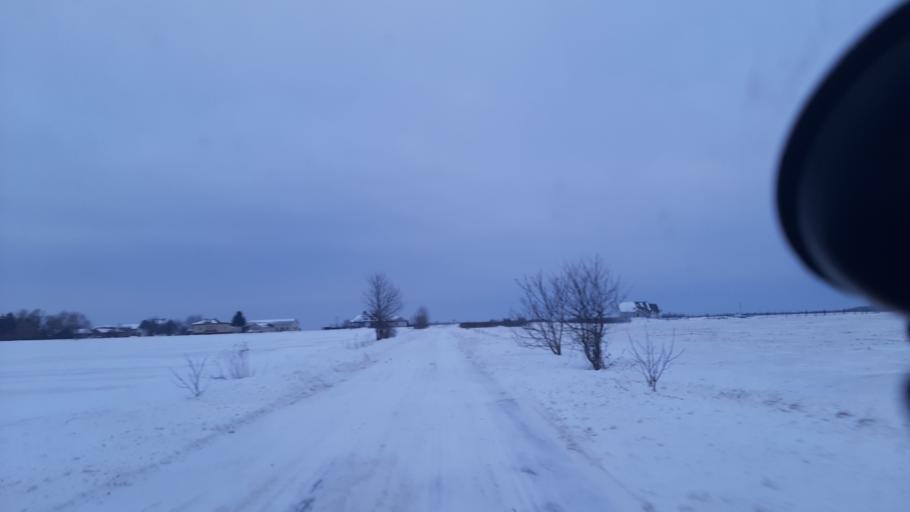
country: PL
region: Lublin Voivodeship
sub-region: Powiat lubelski
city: Jastkow
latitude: 51.3510
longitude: 22.4073
